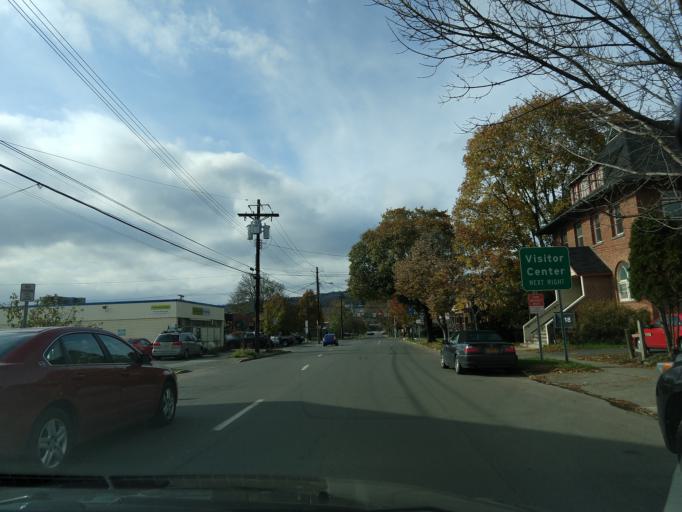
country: US
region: New York
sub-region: Tompkins County
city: Ithaca
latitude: 42.4402
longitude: -76.5071
